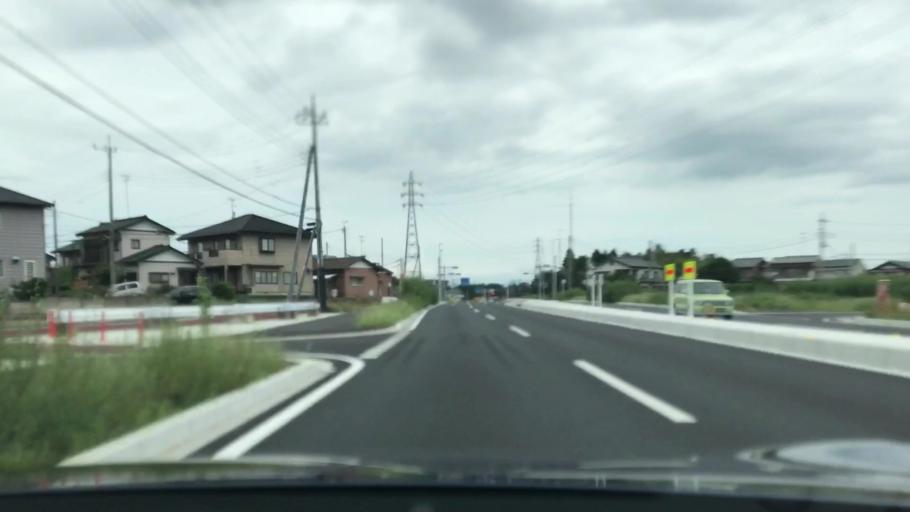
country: JP
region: Gunma
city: Tatebayashi
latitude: 36.2279
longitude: 139.5106
